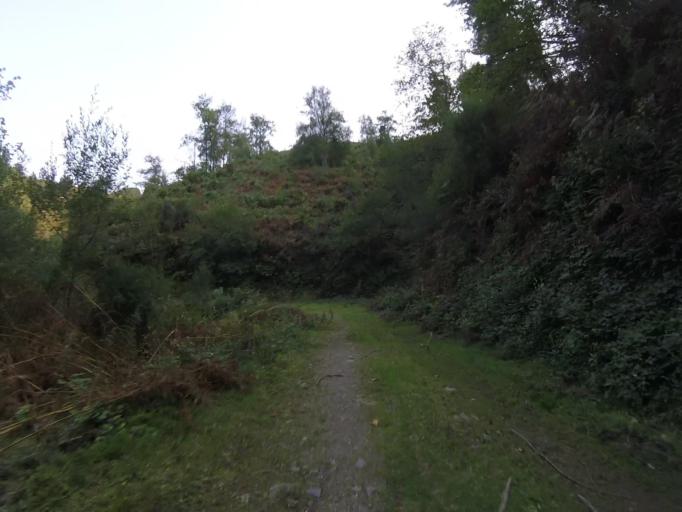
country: ES
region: Navarre
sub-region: Provincia de Navarra
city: Arano
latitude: 43.2522
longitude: -1.8438
